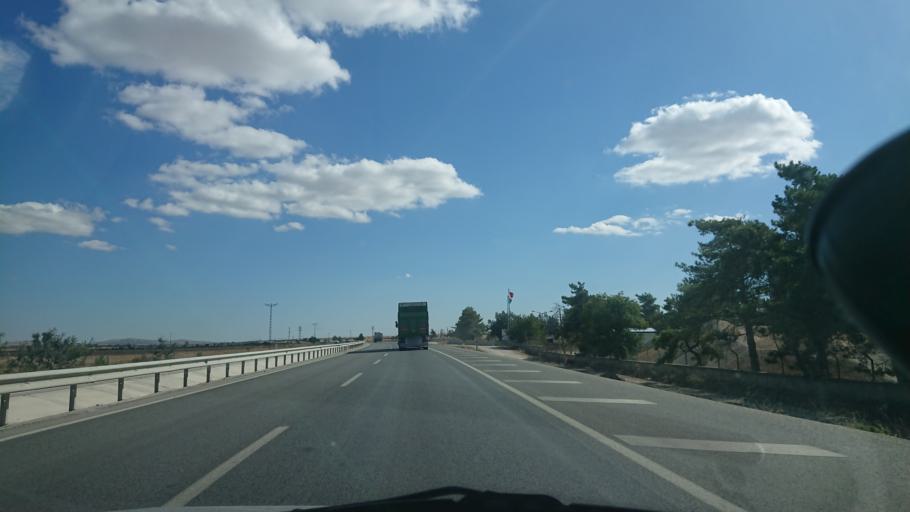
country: TR
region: Eskisehir
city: Mahmudiye
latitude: 39.5619
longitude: 30.9160
